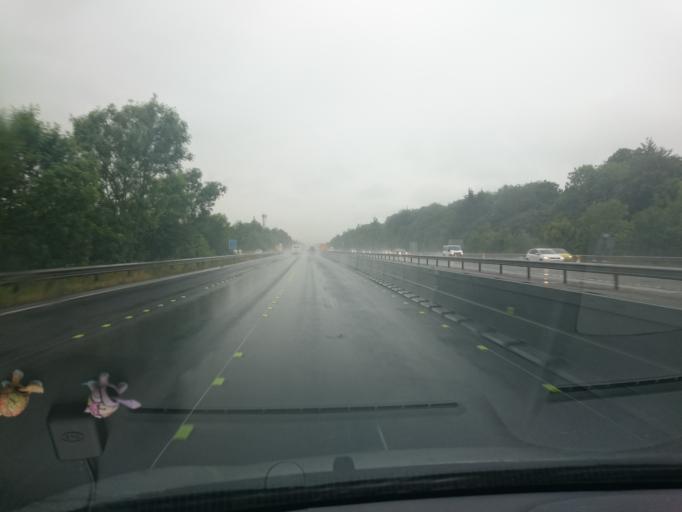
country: GB
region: England
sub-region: Hampshire
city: Basingstoke
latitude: 51.2567
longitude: -1.0676
